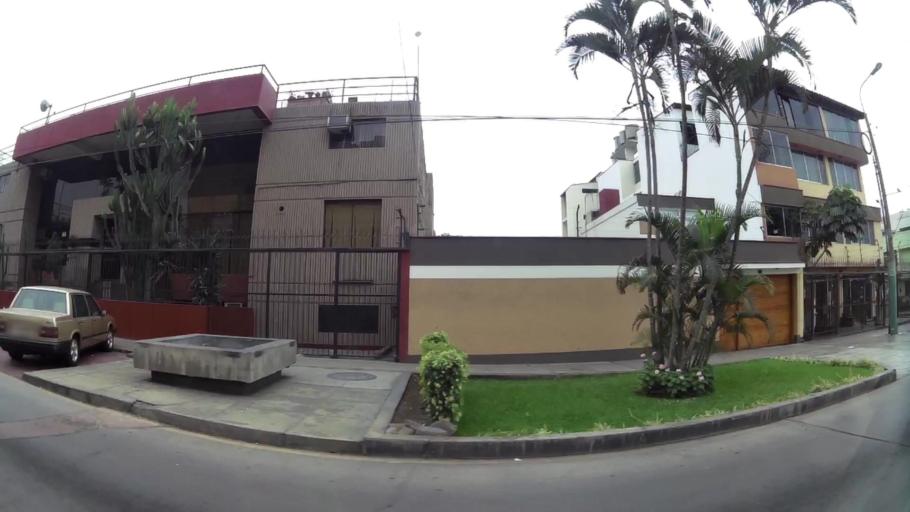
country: PE
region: Lima
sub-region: Lima
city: San Luis
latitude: -12.0900
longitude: -76.9967
